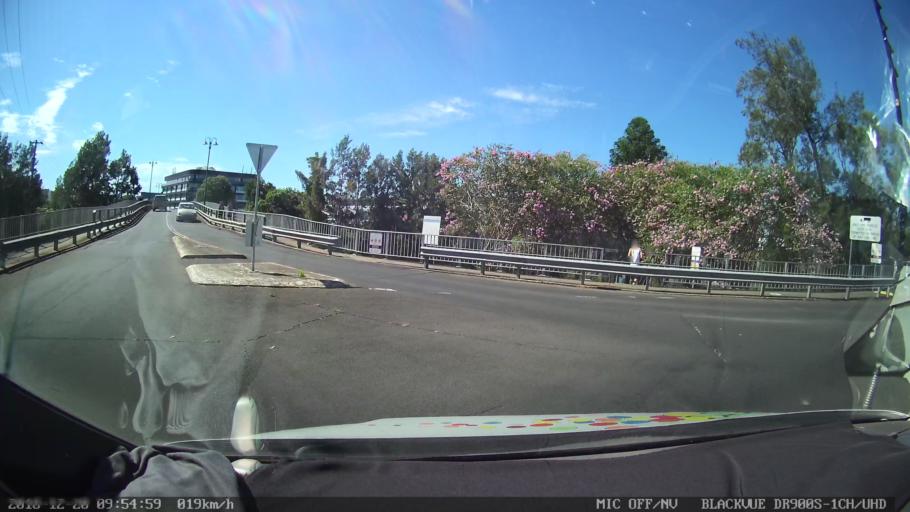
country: AU
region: New South Wales
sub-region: Lismore Municipality
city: Lismore
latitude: -28.8052
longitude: 153.2753
